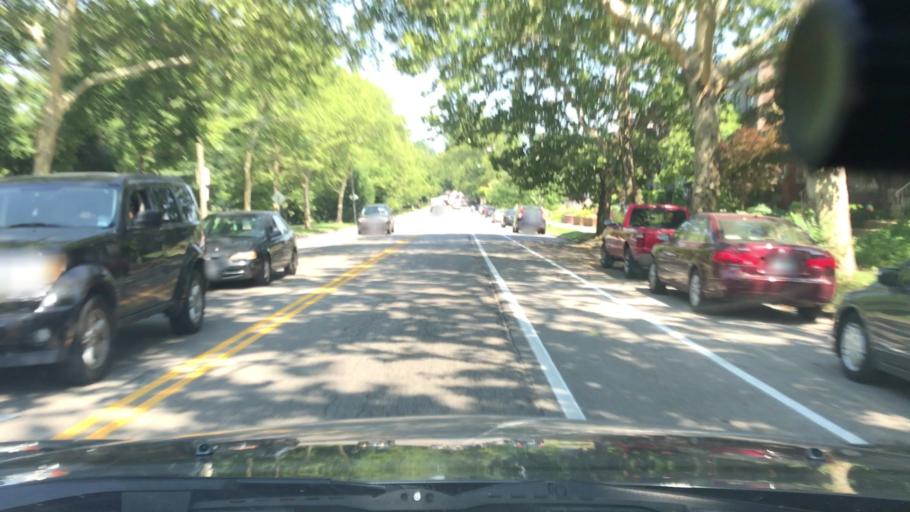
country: US
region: Missouri
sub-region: City of Saint Louis
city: St. Louis
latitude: 38.6040
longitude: -90.2549
